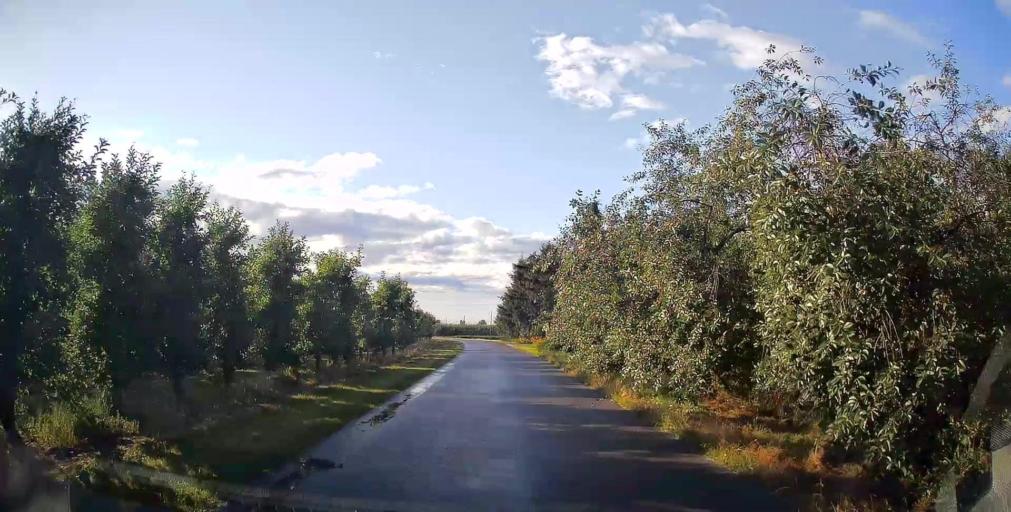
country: PL
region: Masovian Voivodeship
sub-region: Powiat grojecki
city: Goszczyn
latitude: 51.7515
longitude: 20.8847
